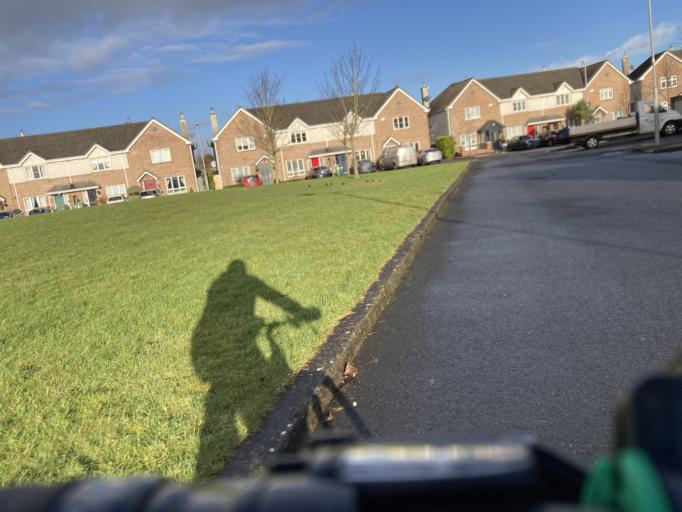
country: IE
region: Leinster
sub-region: Kildare
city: Celbridge
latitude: 53.3481
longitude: -6.5533
